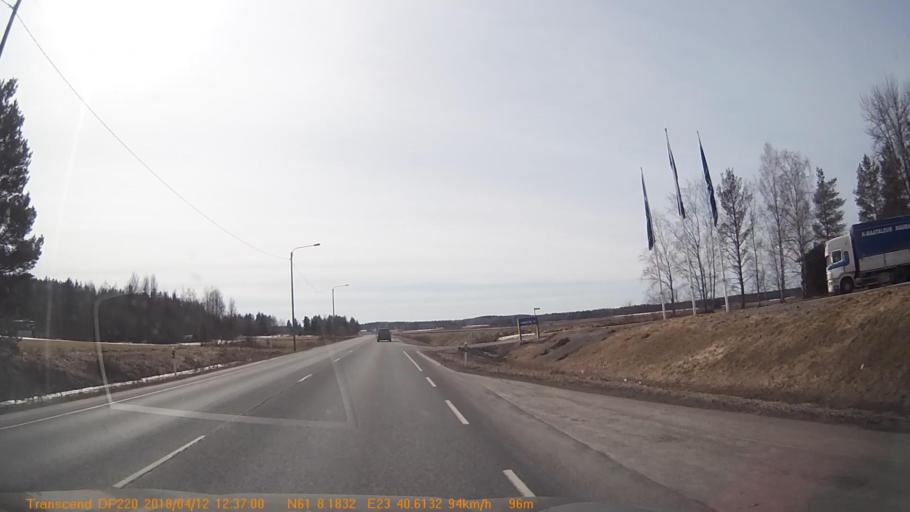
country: FI
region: Pirkanmaa
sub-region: Etelae-Pirkanmaa
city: Kylmaekoski
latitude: 61.1364
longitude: 23.6770
